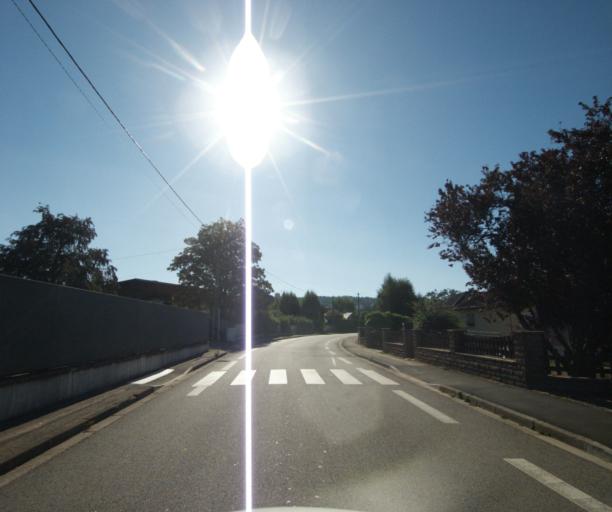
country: FR
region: Lorraine
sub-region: Departement des Vosges
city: Epinal
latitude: 48.1784
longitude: 6.4703
